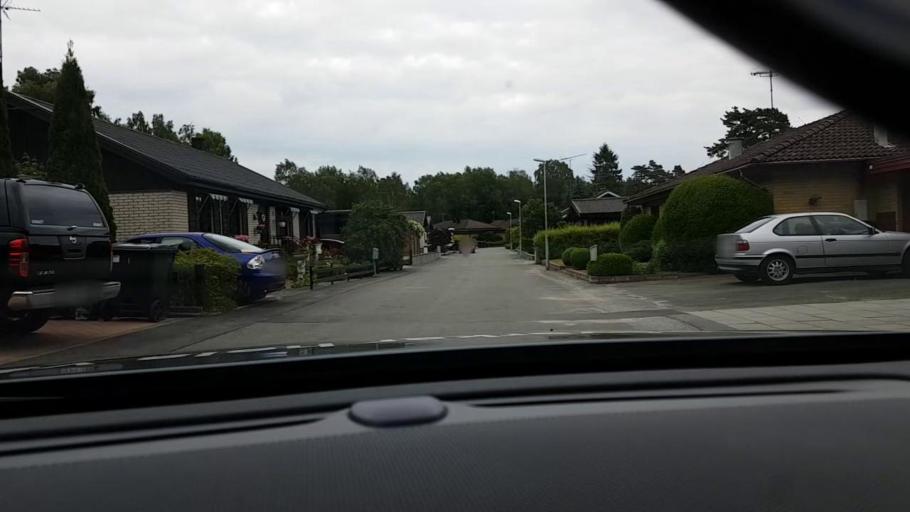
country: SE
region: Skane
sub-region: Hassleholms Kommun
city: Hassleholm
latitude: 56.1730
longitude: 13.7997
